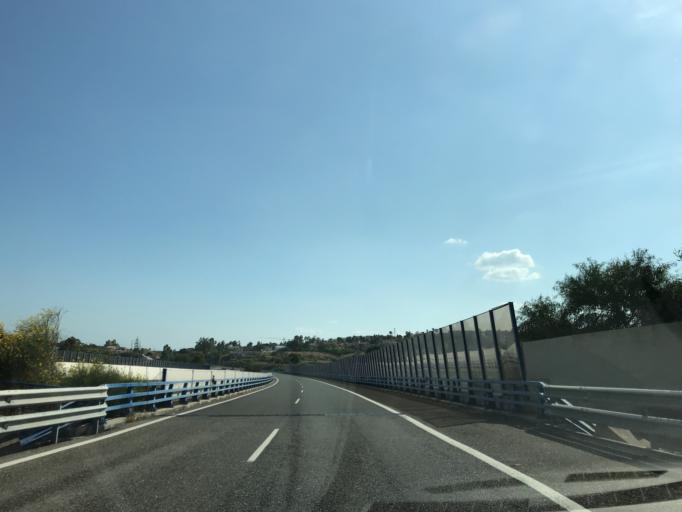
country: ES
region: Andalusia
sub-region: Provincia de Malaga
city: Benahavis
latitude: 36.5131
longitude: -4.9885
